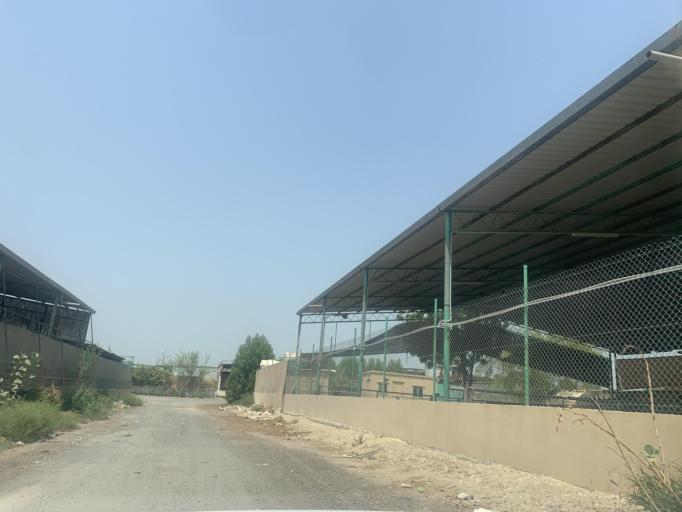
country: BH
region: Central Governorate
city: Madinat Hamad
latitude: 26.1419
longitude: 50.4766
